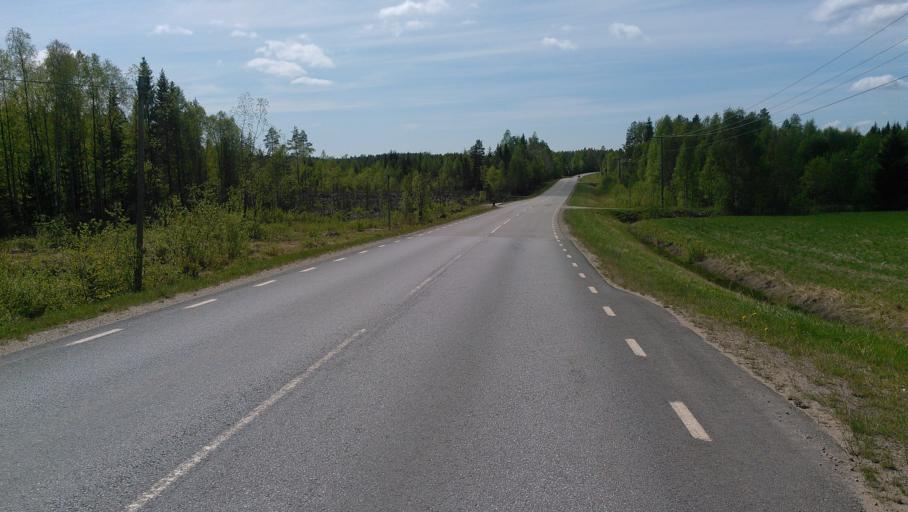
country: SE
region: Vaesterbotten
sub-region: Vannas Kommun
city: Vannasby
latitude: 63.8569
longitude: 19.9997
